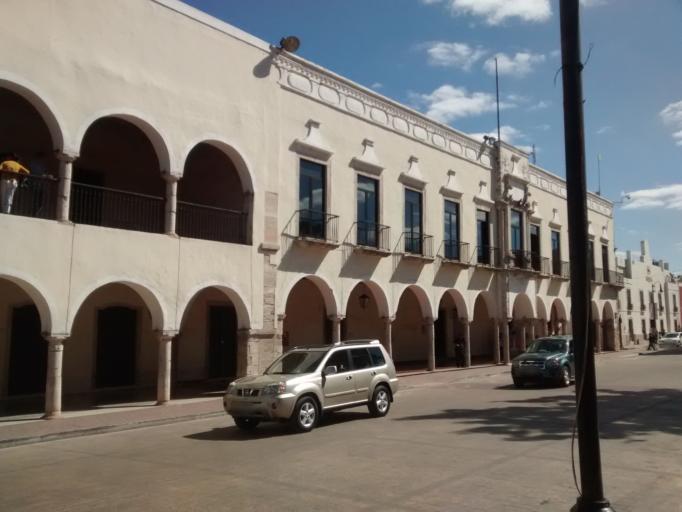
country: MX
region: Yucatan
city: Valladolid
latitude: 20.6902
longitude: -88.2012
